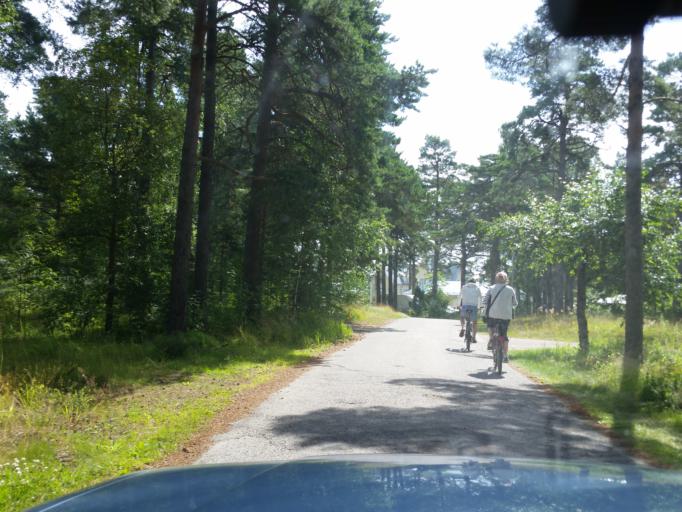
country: FI
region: Uusimaa
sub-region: Raaseporin
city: Hanko
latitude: 59.8294
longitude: 22.9958
